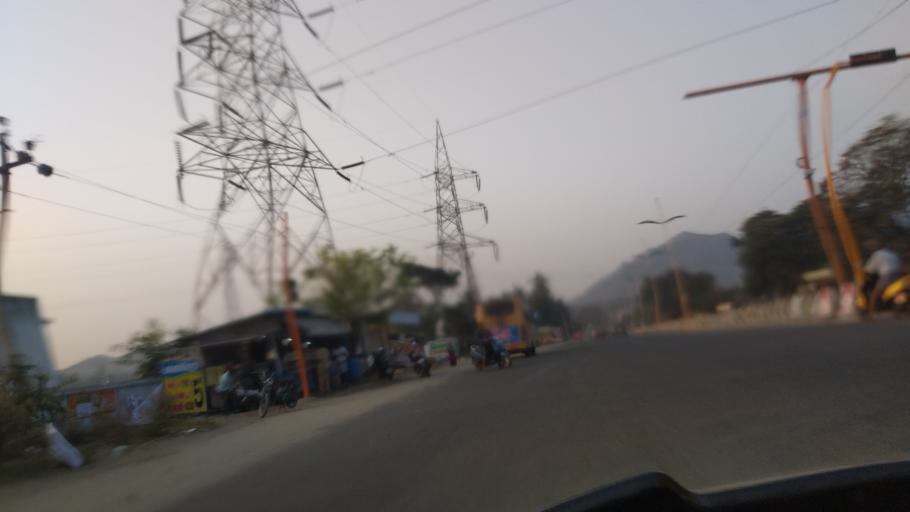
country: IN
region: Tamil Nadu
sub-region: Coimbatore
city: Madukkarai
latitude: 10.9367
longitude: 76.9512
